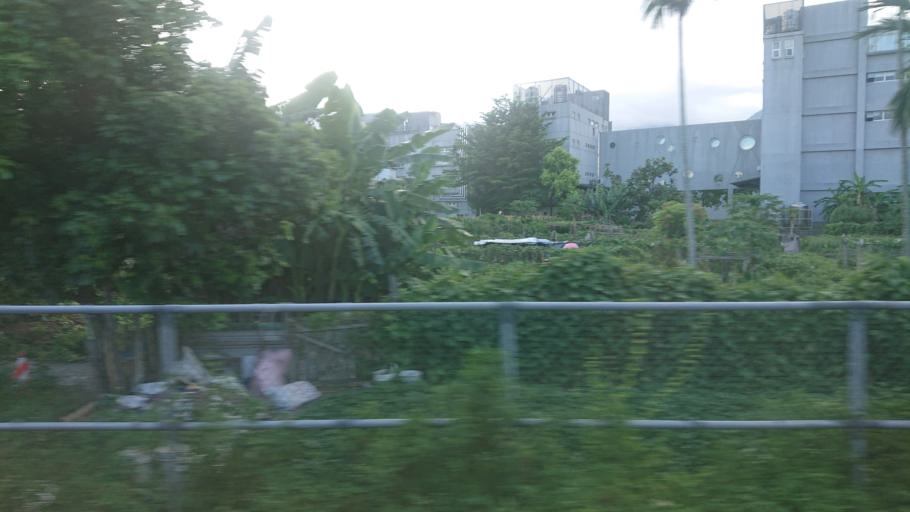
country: TW
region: Taiwan
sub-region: Hualien
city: Hualian
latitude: 23.9767
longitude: 121.5930
